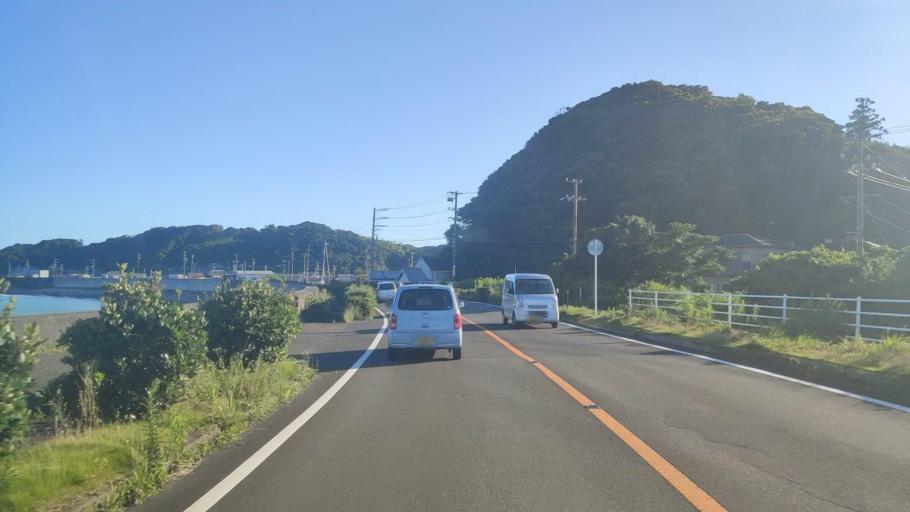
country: JP
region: Mie
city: Toba
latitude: 34.2729
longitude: 136.8689
